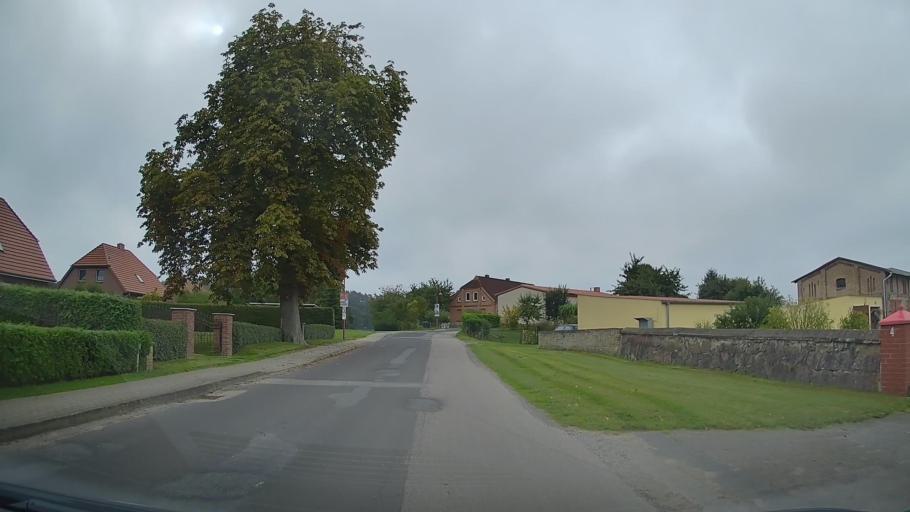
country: DE
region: Mecklenburg-Vorpommern
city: Kavelstorf
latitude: 53.9442
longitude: 12.2143
